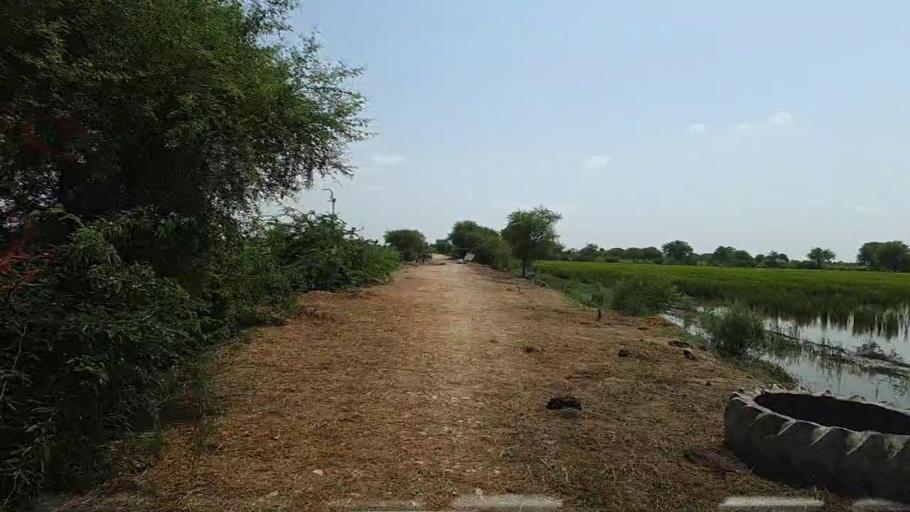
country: PK
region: Sindh
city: Kario
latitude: 24.7018
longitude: 68.6157
